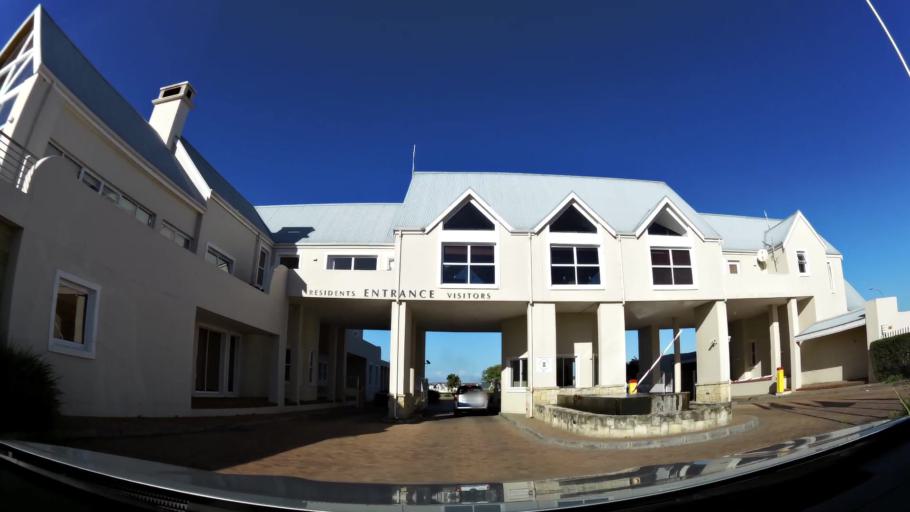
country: ZA
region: Western Cape
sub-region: Eden District Municipality
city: George
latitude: -33.9685
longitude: 22.4294
